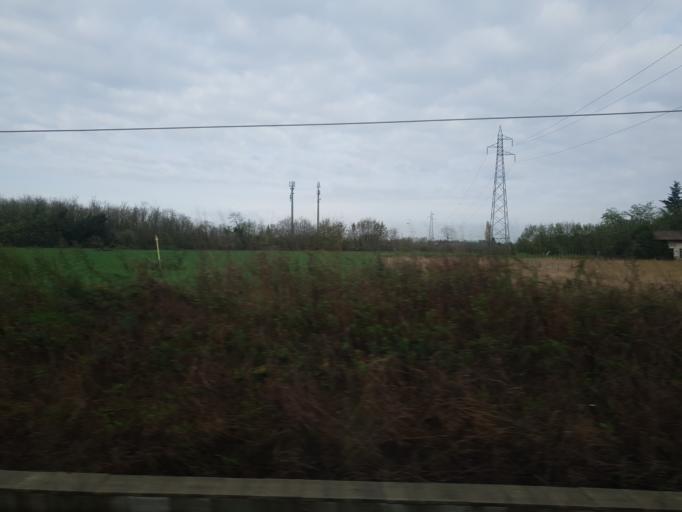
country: IT
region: Lombardy
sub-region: Provincia di Varese
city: Cascina Elisa
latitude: 45.5991
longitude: 8.8097
